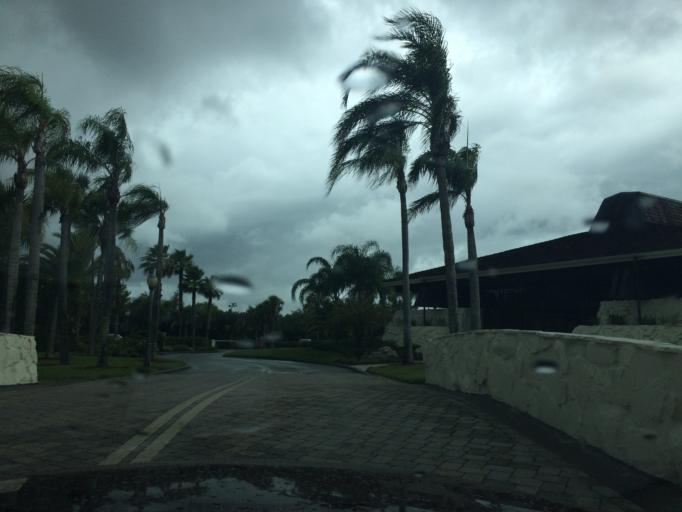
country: US
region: Florida
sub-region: Pasco County
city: Wesley Chapel
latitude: 28.2267
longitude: -82.3281
